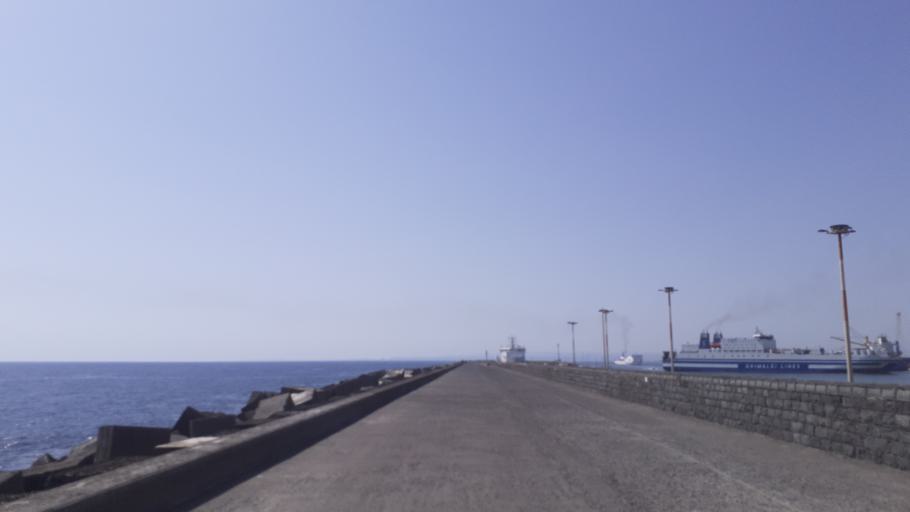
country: IT
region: Sicily
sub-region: Catania
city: Catania
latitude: 37.4991
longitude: 15.0991
